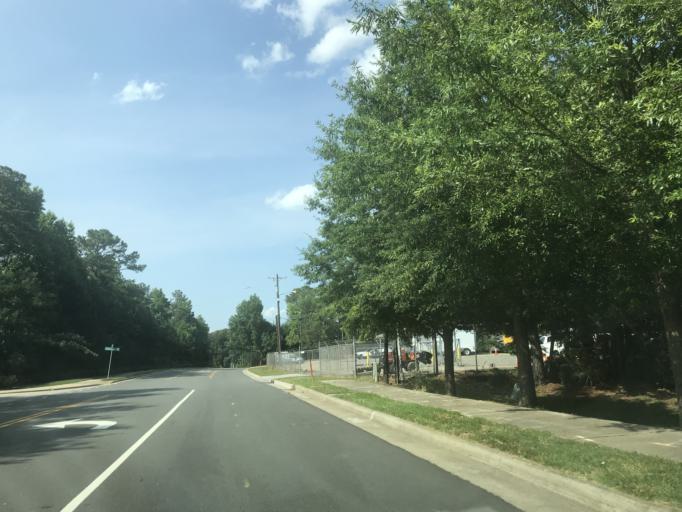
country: US
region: North Carolina
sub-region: Wake County
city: Cary
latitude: 35.7957
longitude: -78.7349
